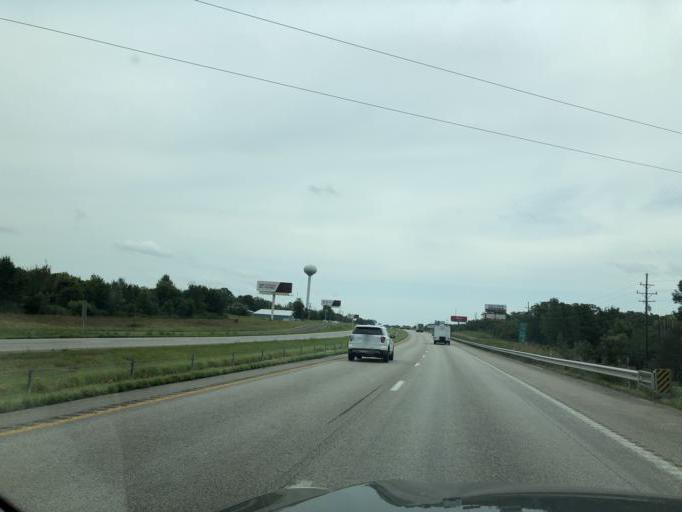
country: US
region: Missouri
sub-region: Warren County
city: Warrenton
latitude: 38.8269
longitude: -91.2082
